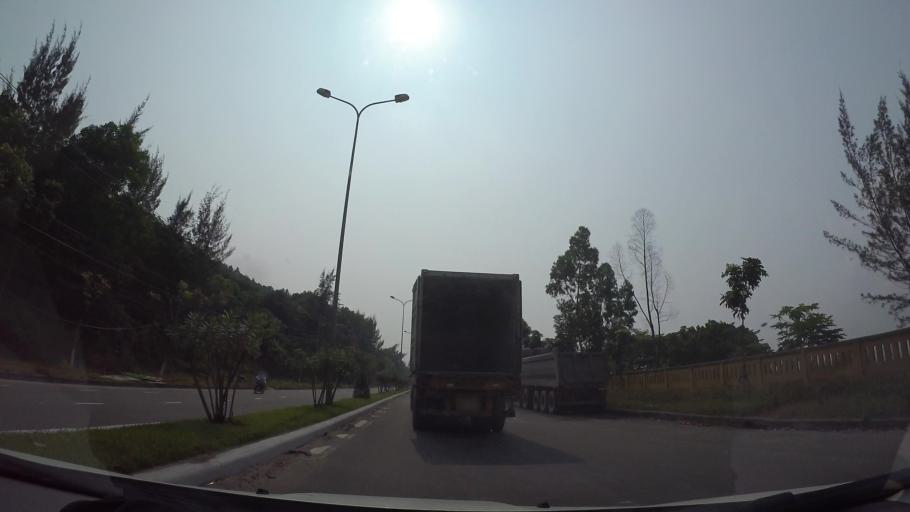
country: VN
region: Da Nang
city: Da Nang
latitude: 16.1160
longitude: 108.2331
